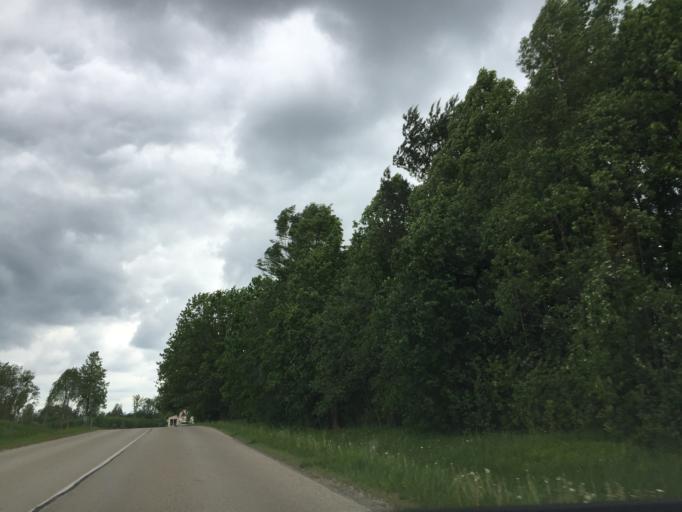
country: LV
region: Dagda
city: Dagda
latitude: 56.1166
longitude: 27.4767
